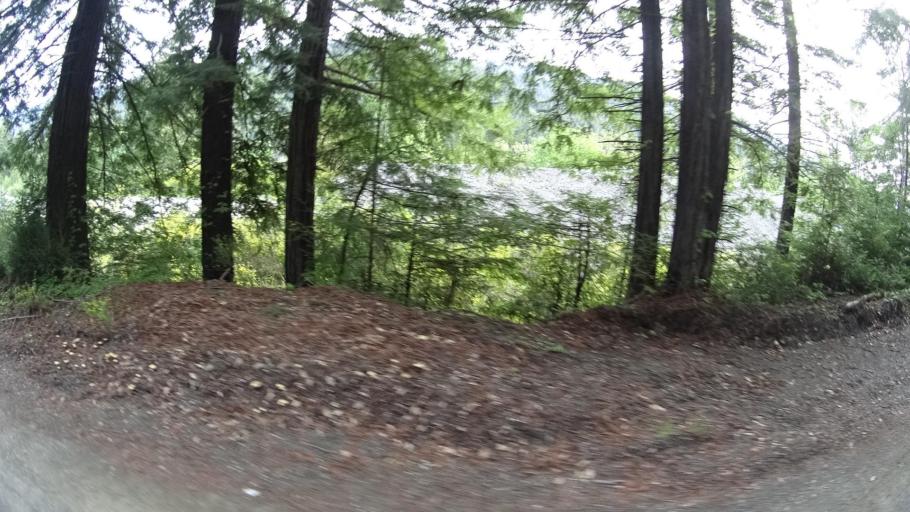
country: US
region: California
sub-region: Humboldt County
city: Redway
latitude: 40.3231
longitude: -123.8363
